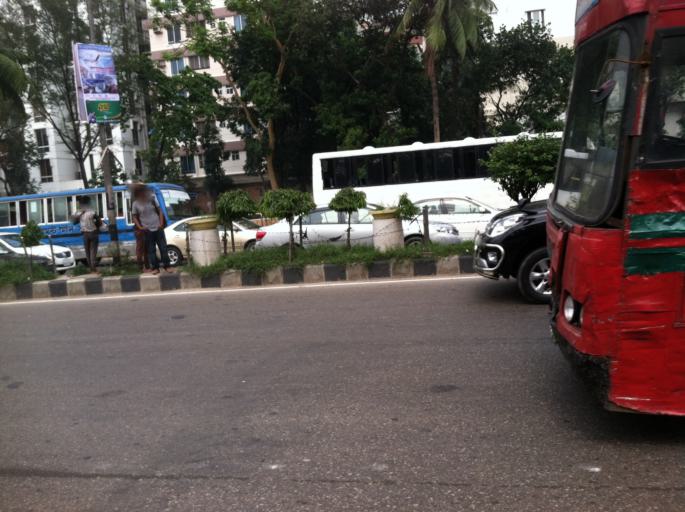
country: BD
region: Dhaka
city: Paltan
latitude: 23.7950
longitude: 90.4010
